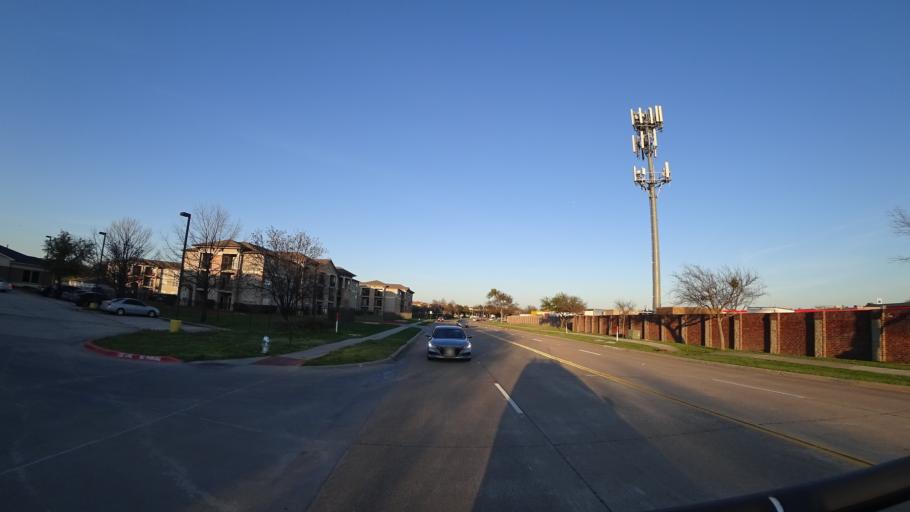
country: US
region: Texas
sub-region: Dallas County
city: Coppell
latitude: 32.9940
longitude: -96.9780
